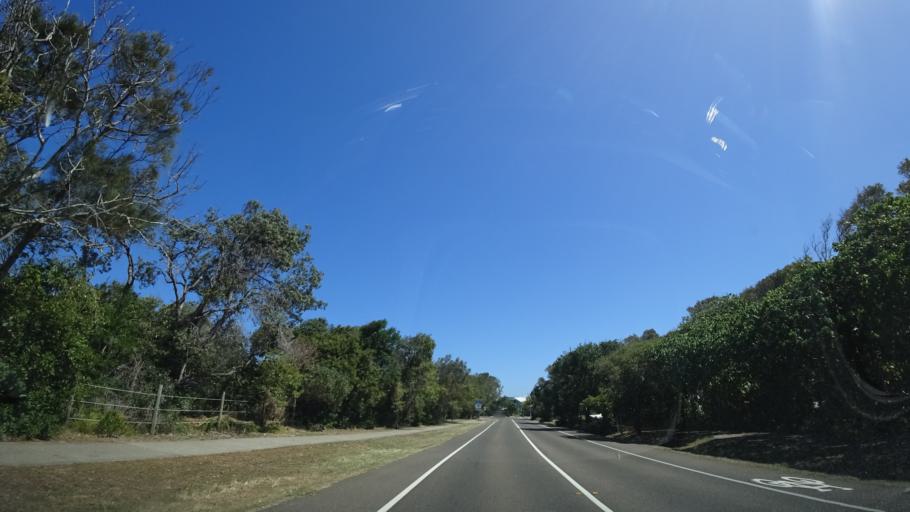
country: AU
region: Queensland
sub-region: Sunshine Coast
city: Mooloolaba
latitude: -26.6094
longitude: 153.0992
